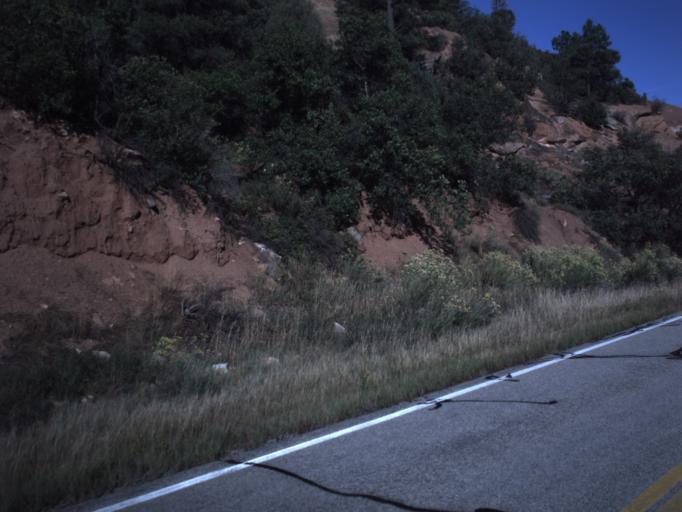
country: US
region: Utah
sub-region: San Juan County
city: Monticello
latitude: 38.3283
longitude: -109.0749
